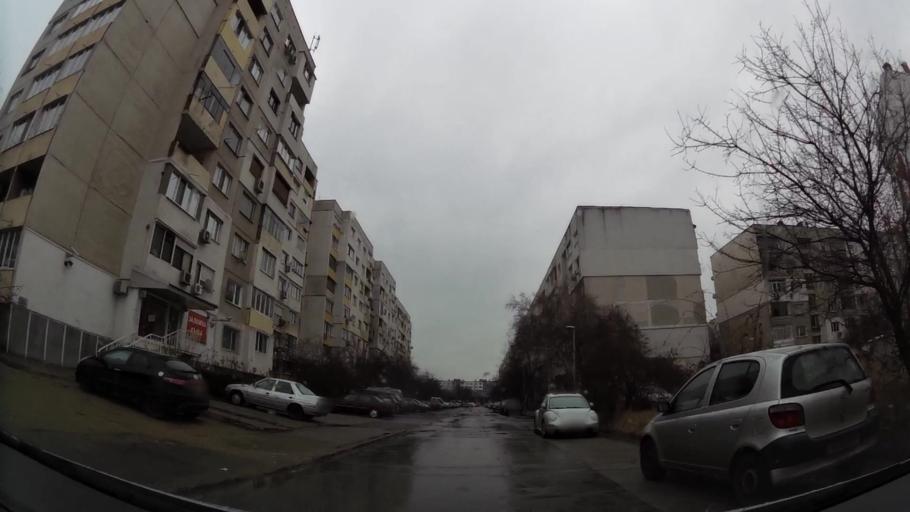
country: BG
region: Sofia-Capital
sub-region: Stolichna Obshtina
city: Sofia
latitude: 42.6669
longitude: 23.3891
